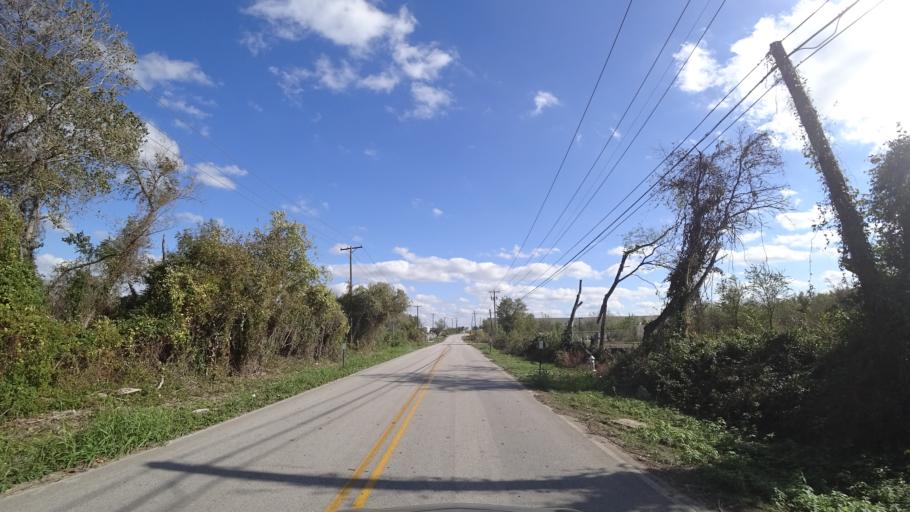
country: US
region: Texas
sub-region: Travis County
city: Wells Branch
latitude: 30.4659
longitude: -97.6757
